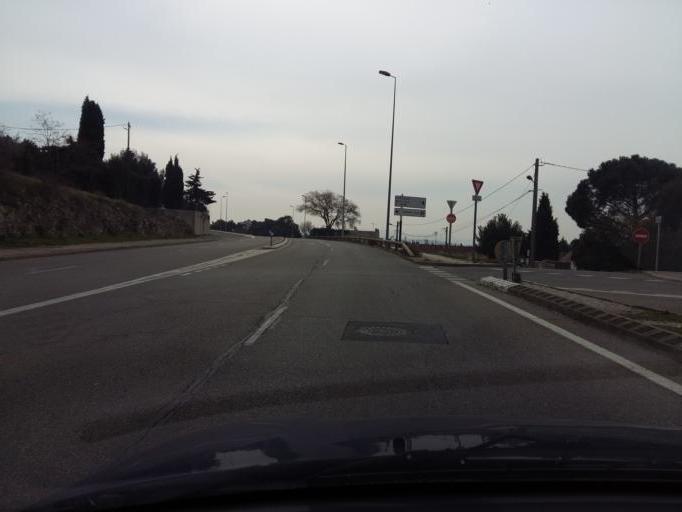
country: FR
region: Provence-Alpes-Cote d'Azur
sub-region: Departement des Bouches-du-Rhone
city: Chateaurenard
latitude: 43.8768
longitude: 4.8490
